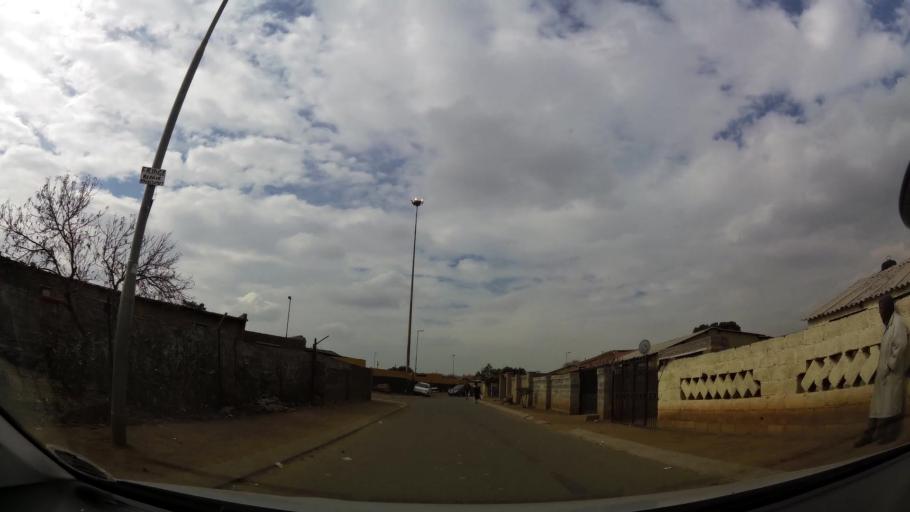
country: ZA
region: Gauteng
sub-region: City of Johannesburg Metropolitan Municipality
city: Soweto
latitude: -26.2691
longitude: 27.8557
